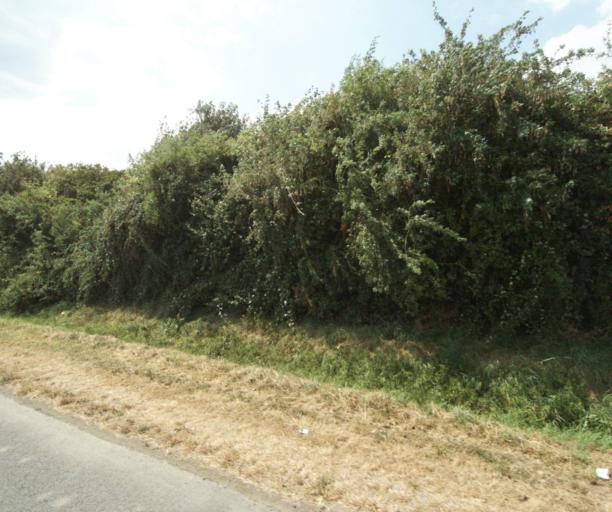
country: FR
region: Nord-Pas-de-Calais
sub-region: Departement du Nord
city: Comines
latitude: 50.7600
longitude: 3.0285
